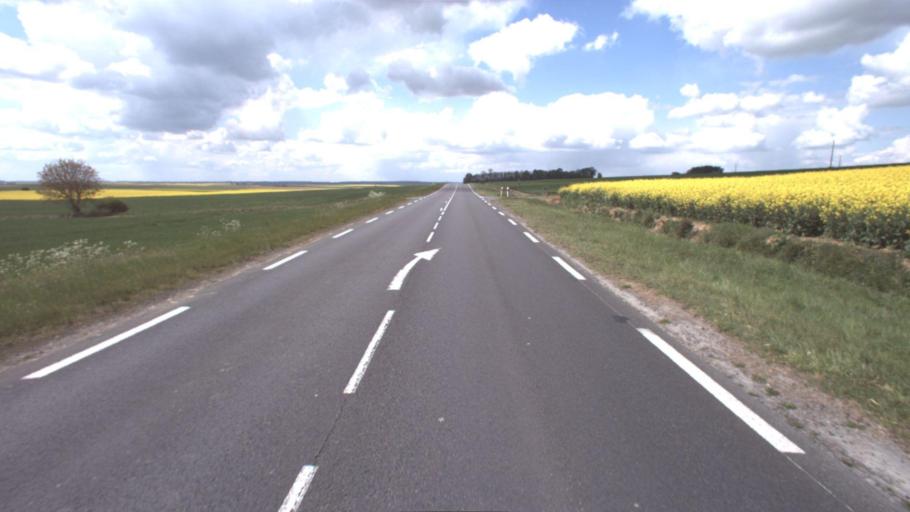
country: FR
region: Ile-de-France
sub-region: Departement de Seine-et-Marne
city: Villiers-Saint-Georges
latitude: 48.6922
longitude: 3.4252
